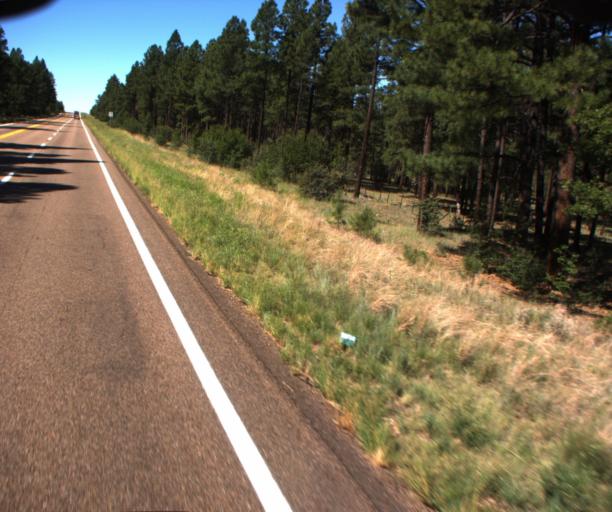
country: US
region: Arizona
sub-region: Navajo County
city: Linden
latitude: 34.0953
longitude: -110.1713
